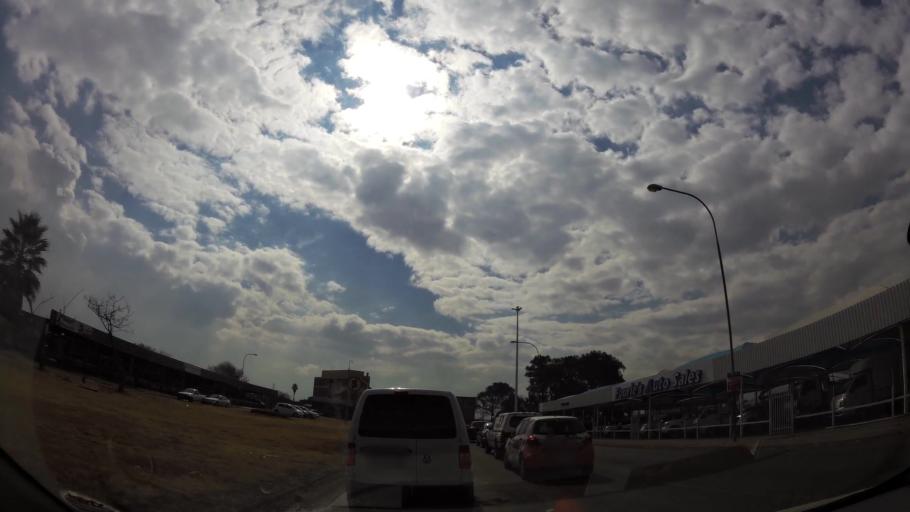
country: ZA
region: Gauteng
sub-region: Sedibeng District Municipality
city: Vereeniging
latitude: -26.6653
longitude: 27.9205
